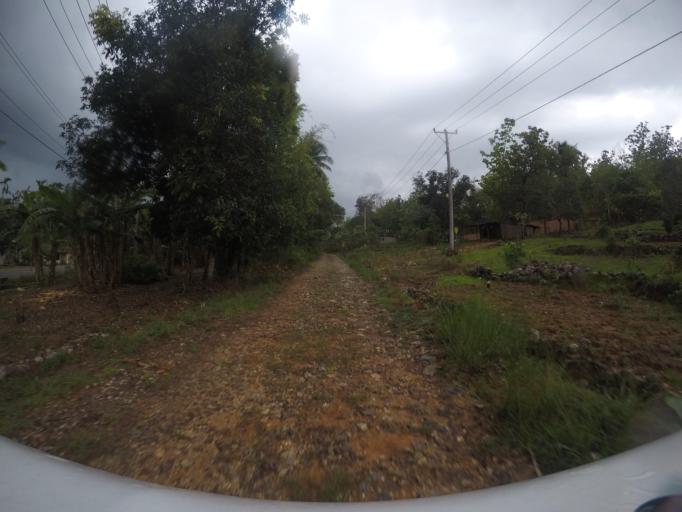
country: TL
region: Bobonaro
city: Maliana
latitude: -8.9572
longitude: 125.2129
